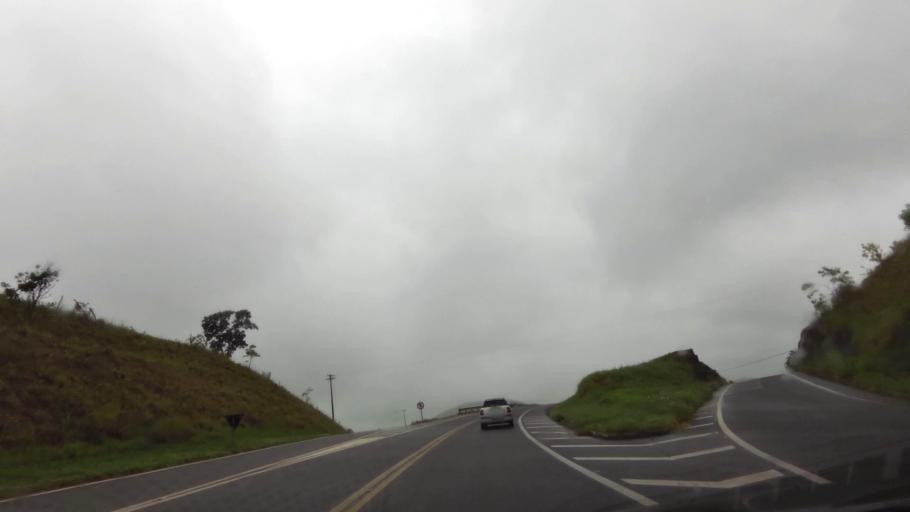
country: BR
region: Espirito Santo
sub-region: Guarapari
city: Guarapari
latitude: -20.7327
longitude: -40.5575
